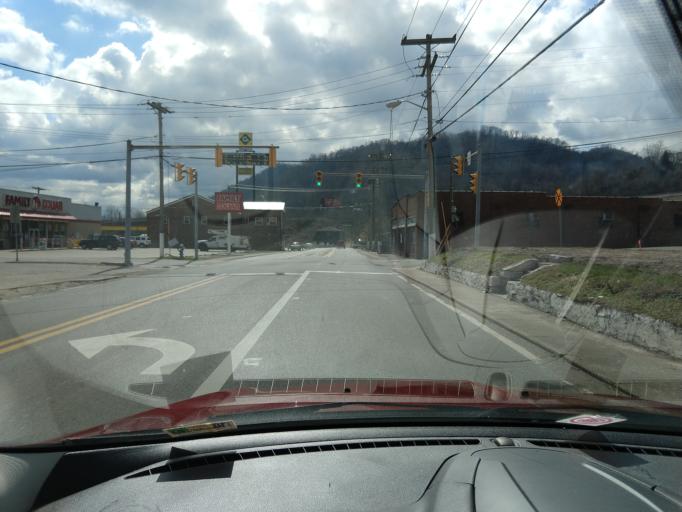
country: US
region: West Virginia
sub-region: Kanawha County
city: Marmet
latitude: 38.2434
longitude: -81.5663
